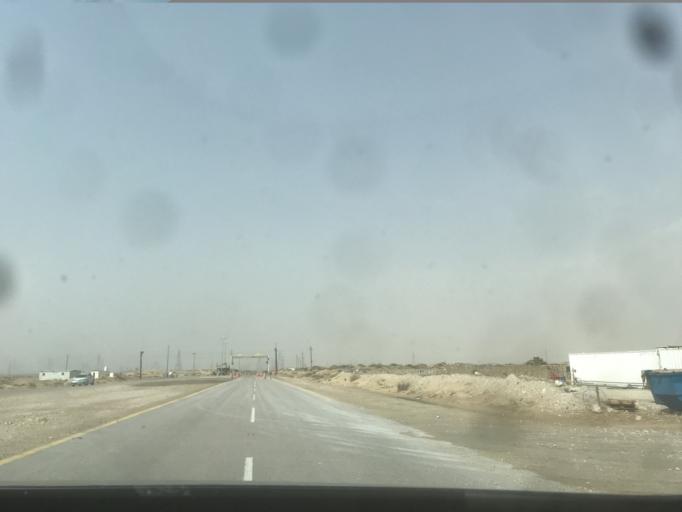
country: SA
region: Eastern Province
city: Abqaiq
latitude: 25.9335
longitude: 49.7338
